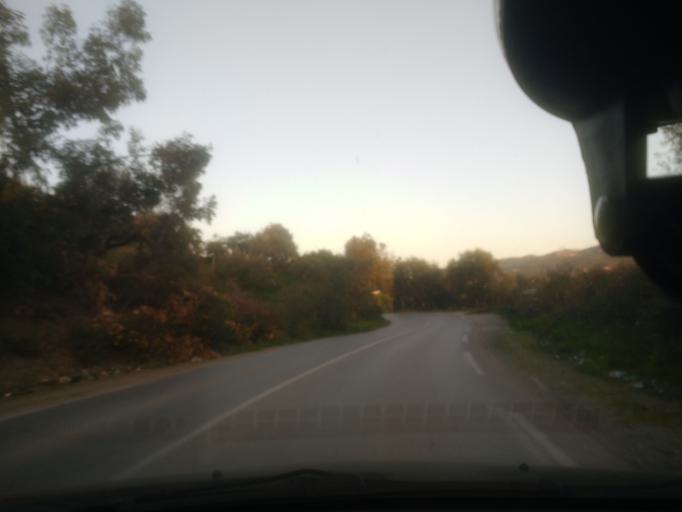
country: DZ
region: Boumerdes
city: Makouda
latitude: 36.7806
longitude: 4.0666
